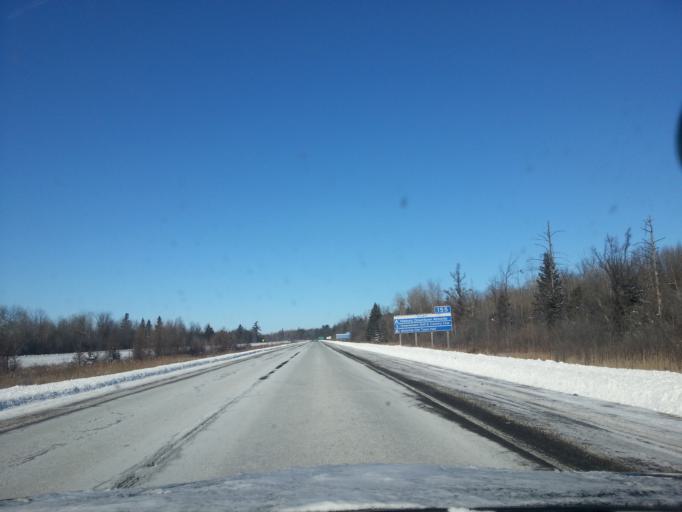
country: CA
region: Ontario
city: Bells Corners
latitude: 45.3032
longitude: -76.0318
